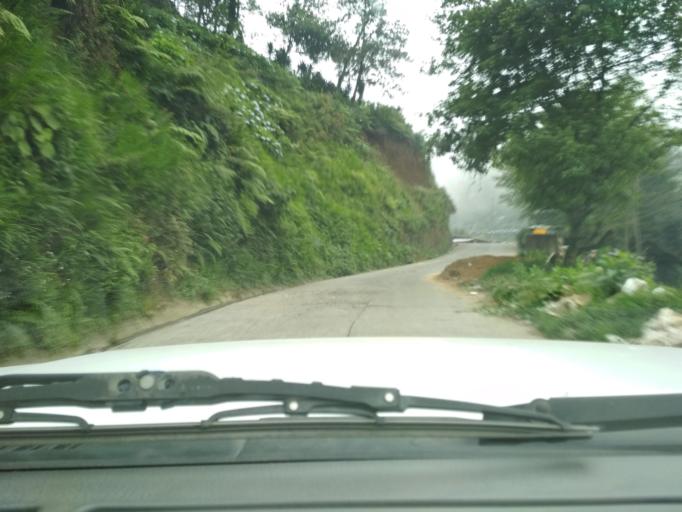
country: MX
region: Veracruz
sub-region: La Perla
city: Metlac Hernandez (Metlac Primero)
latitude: 18.9727
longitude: -97.1471
